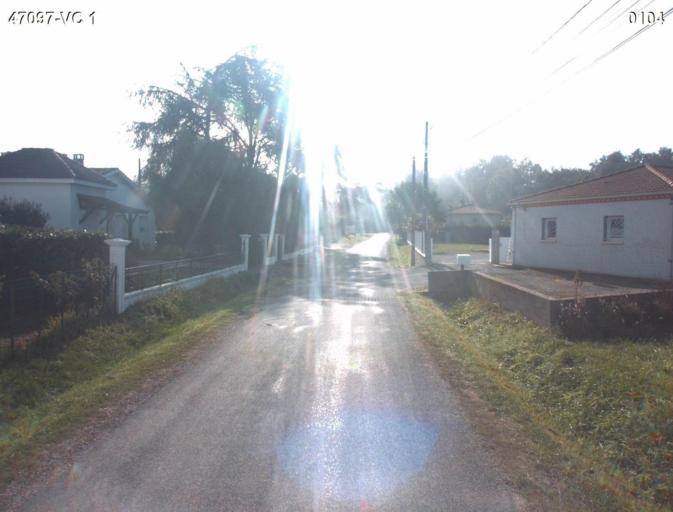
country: FR
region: Aquitaine
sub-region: Departement du Lot-et-Garonne
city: Vianne
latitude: 44.2205
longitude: 0.3472
